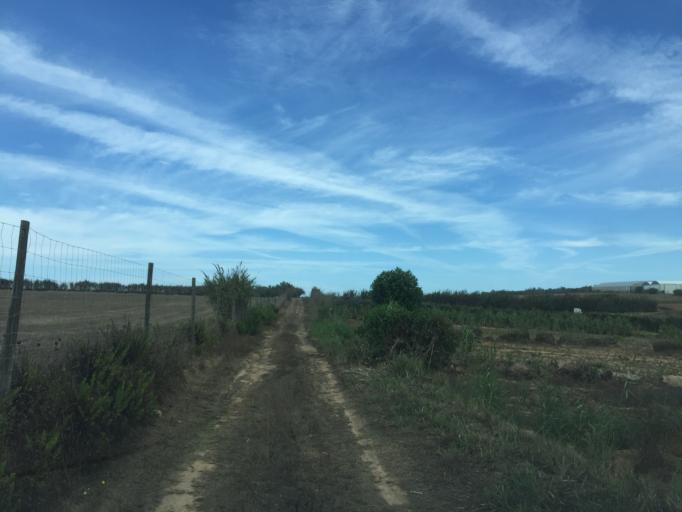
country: PT
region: Lisbon
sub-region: Lourinha
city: Lourinha
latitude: 39.1869
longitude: -9.3481
